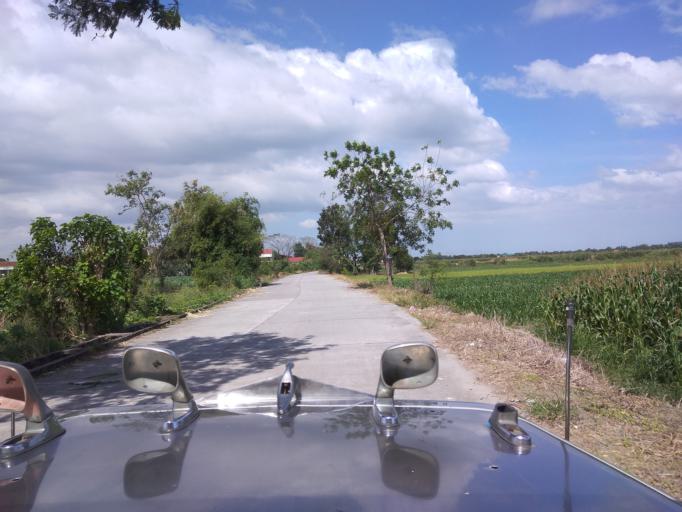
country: PH
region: Central Luzon
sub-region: Province of Pampanga
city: Anao
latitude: 15.1273
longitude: 120.7013
